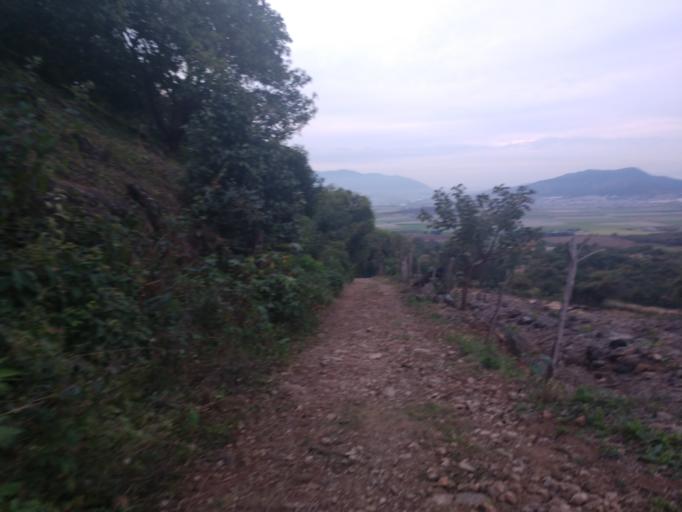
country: MX
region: Nayarit
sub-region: Tepic
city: La Corregidora
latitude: 21.4686
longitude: -104.7857
